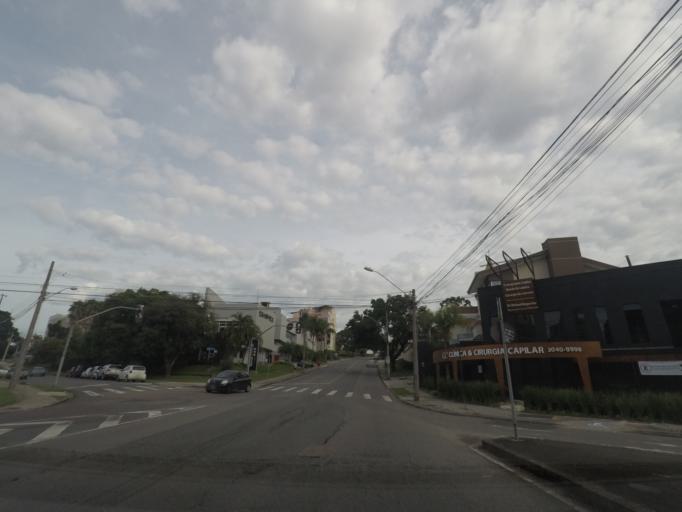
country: BR
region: Parana
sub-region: Curitiba
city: Curitiba
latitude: -25.4275
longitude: -49.2975
